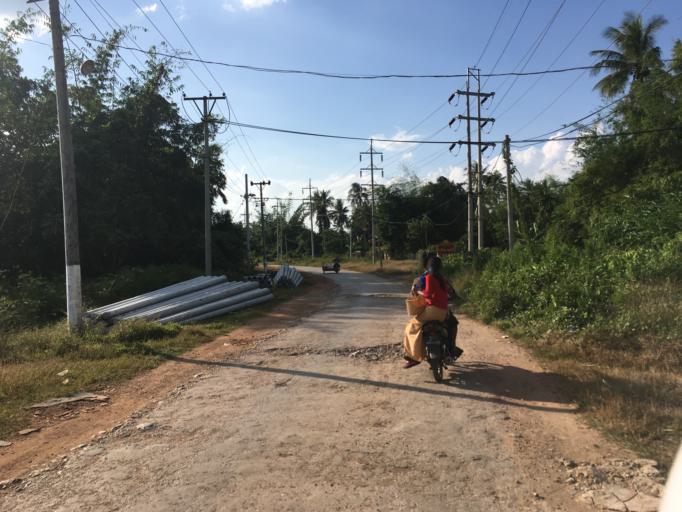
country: MM
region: Mon
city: Mawlamyine
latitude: 16.4280
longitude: 97.6308
